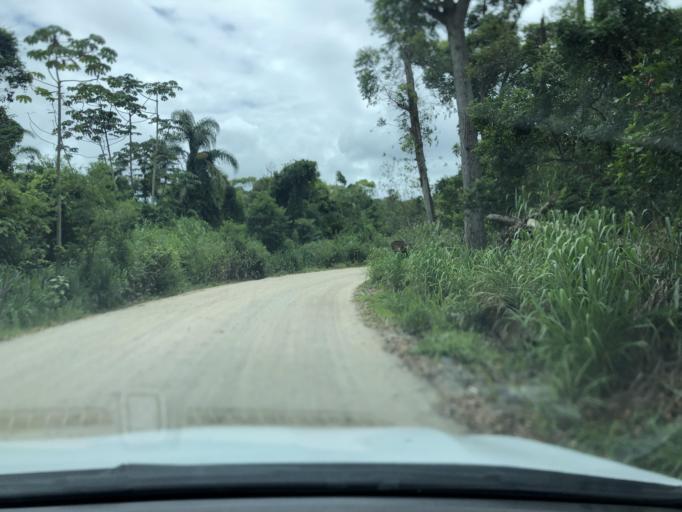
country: BR
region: Santa Catarina
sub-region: Florianopolis
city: Lagoa
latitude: -27.5236
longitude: -48.4204
